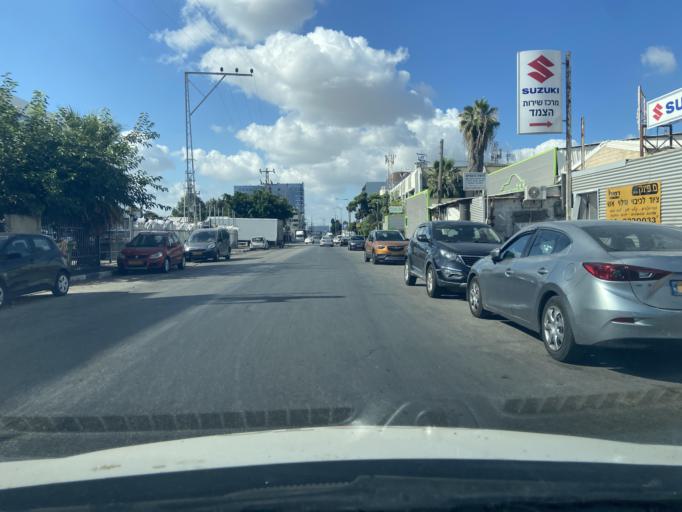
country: IL
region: Central District
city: Yehud
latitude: 32.0301
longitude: 34.8992
